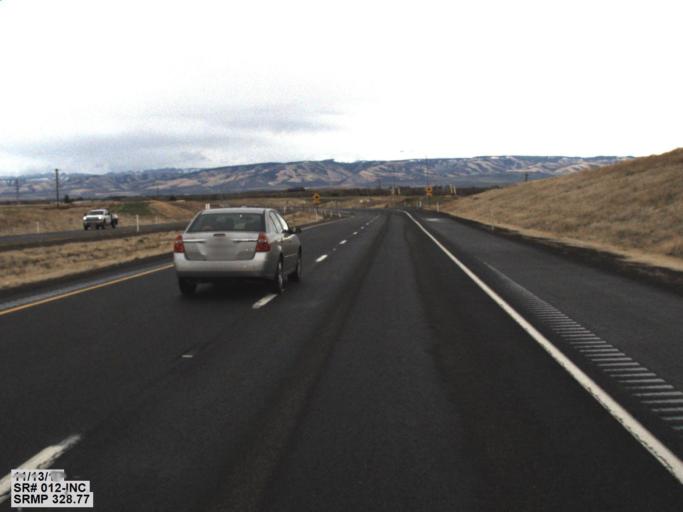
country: US
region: Washington
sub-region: Walla Walla County
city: Garrett
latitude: 46.0500
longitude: -118.4958
